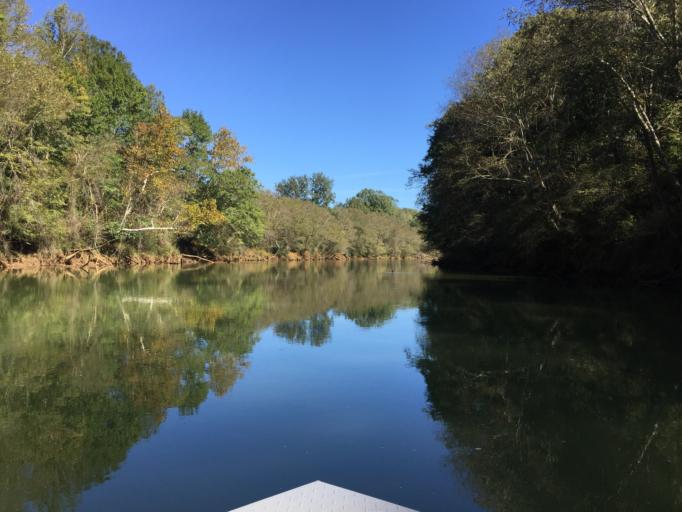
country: US
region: Georgia
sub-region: Gwinnett County
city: Suwanee
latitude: 34.0392
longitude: -84.1144
